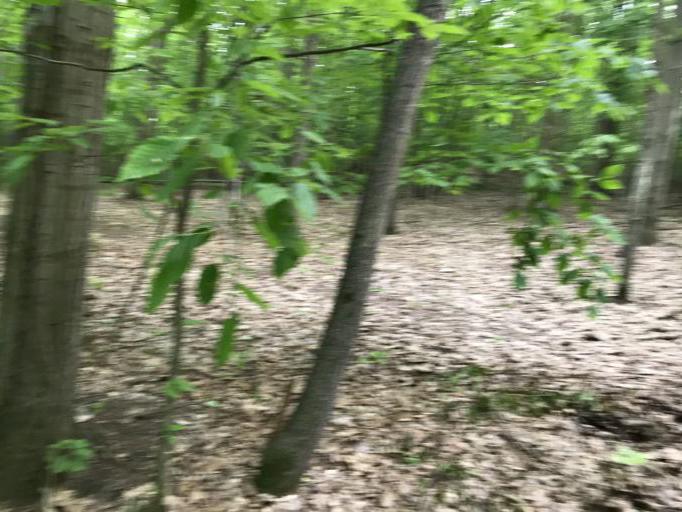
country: US
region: Michigan
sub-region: Oakland County
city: Farmington Hills
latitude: 42.4770
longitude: -83.3869
